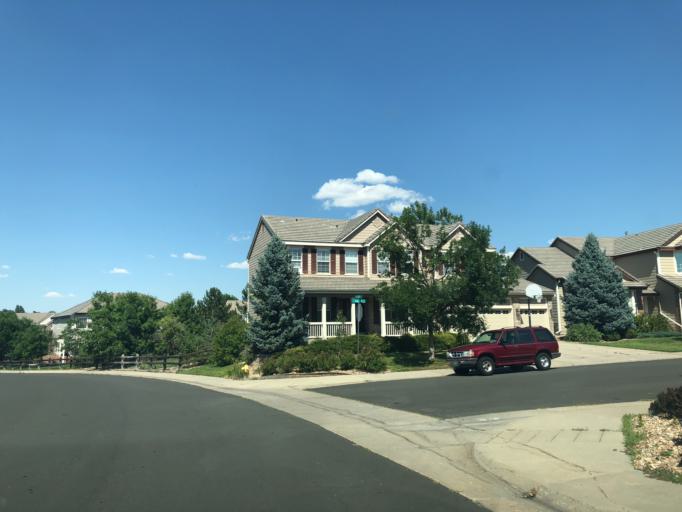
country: US
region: Colorado
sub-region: Arapahoe County
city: Dove Valley
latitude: 39.6073
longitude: -104.7843
